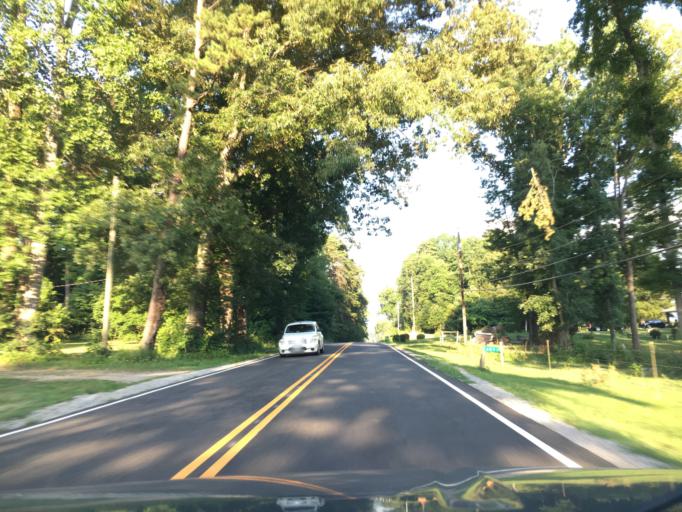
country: US
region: Virginia
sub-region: Pittsylvania County
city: Chatham
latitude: 36.8186
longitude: -79.3619
